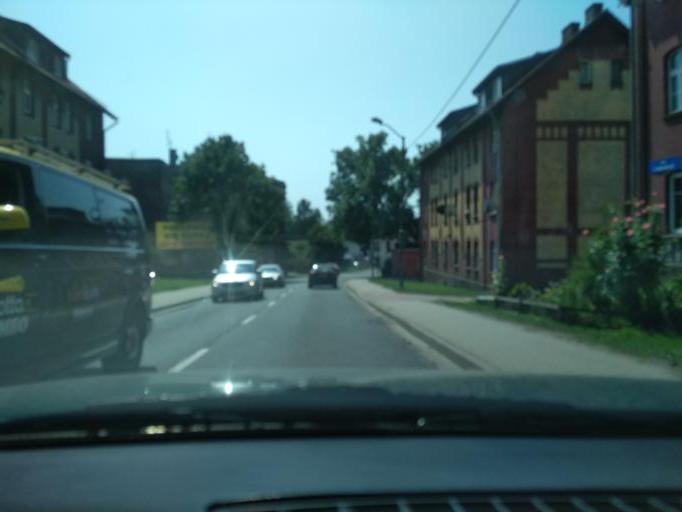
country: PL
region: Silesian Voivodeship
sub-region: Katowice
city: Katowice
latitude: 50.2805
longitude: 19.0062
